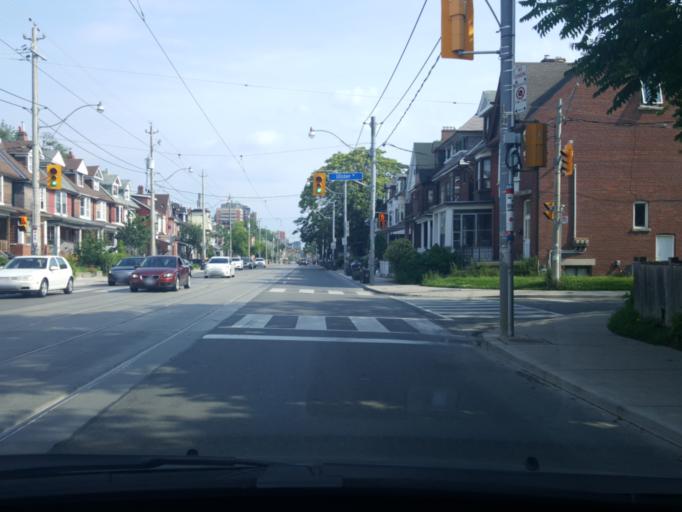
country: CA
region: Ontario
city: Toronto
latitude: 43.6600
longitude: -79.4092
